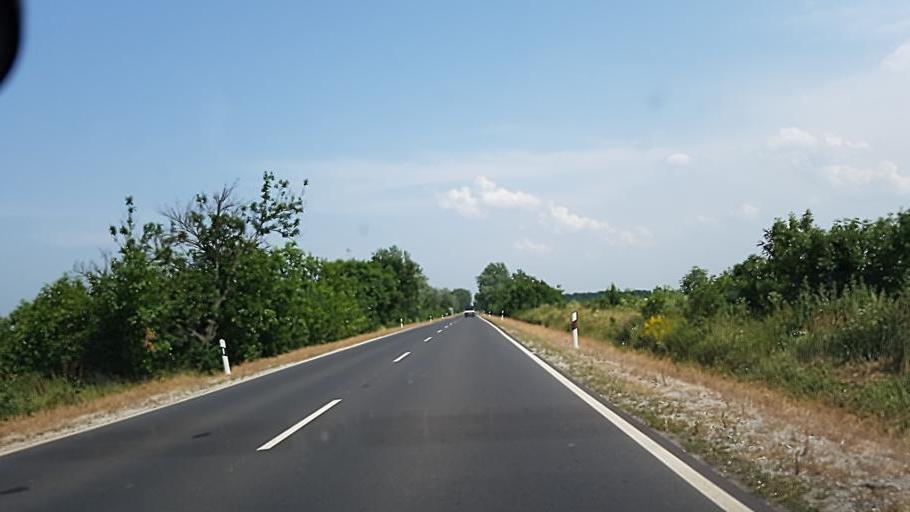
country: HU
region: Heves
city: Poroszlo
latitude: 47.6493
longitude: 20.6230
